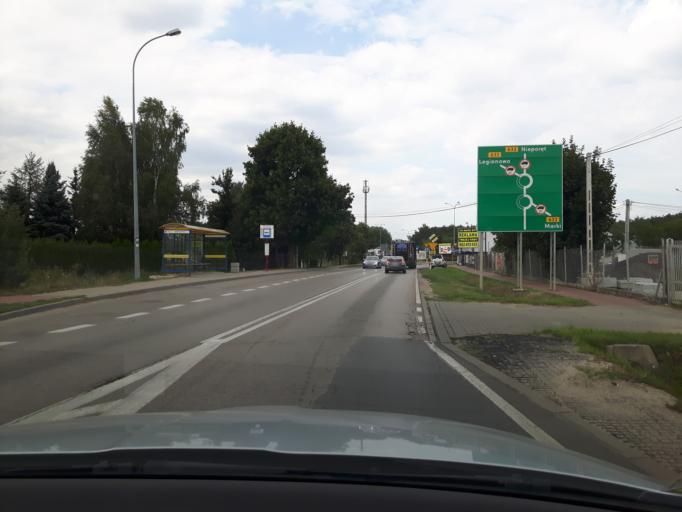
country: PL
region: Masovian Voivodeship
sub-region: Powiat legionowski
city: Stanislawow Pierwszy
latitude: 52.3771
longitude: 21.0292
